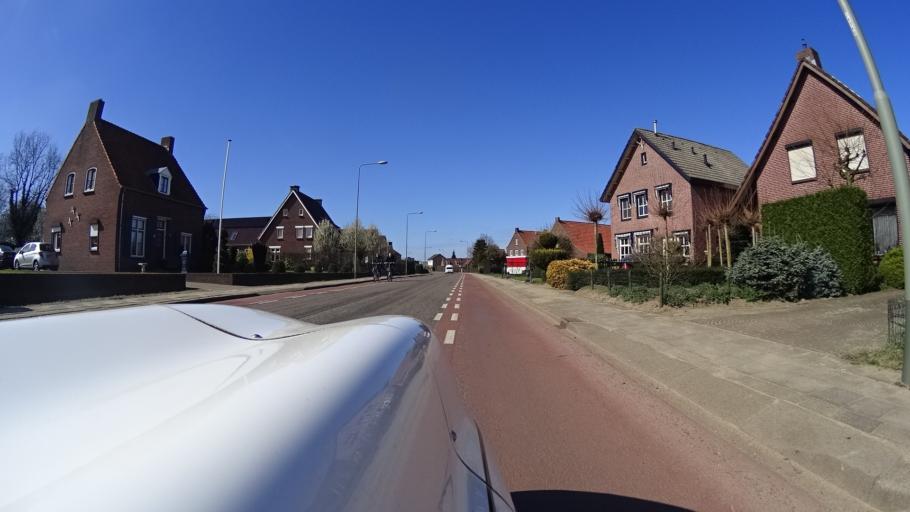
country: NL
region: Limburg
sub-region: Gemeente Bergen
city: Wellerlooi
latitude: 51.5308
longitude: 6.1053
